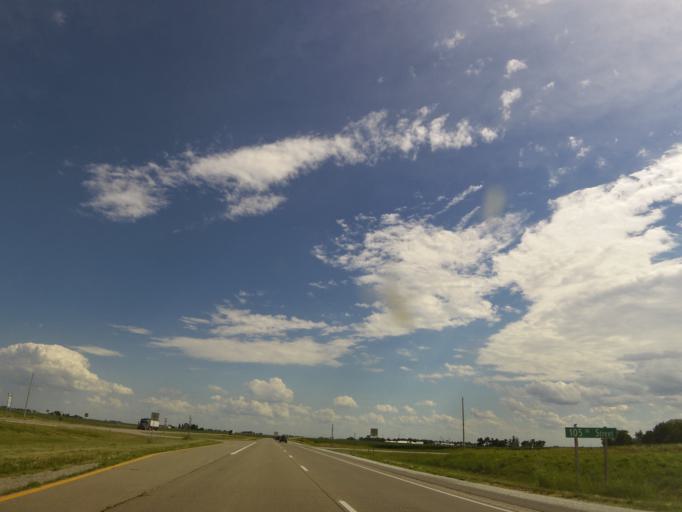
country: US
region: Iowa
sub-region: Henry County
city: Winfield
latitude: 41.1578
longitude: -91.5411
